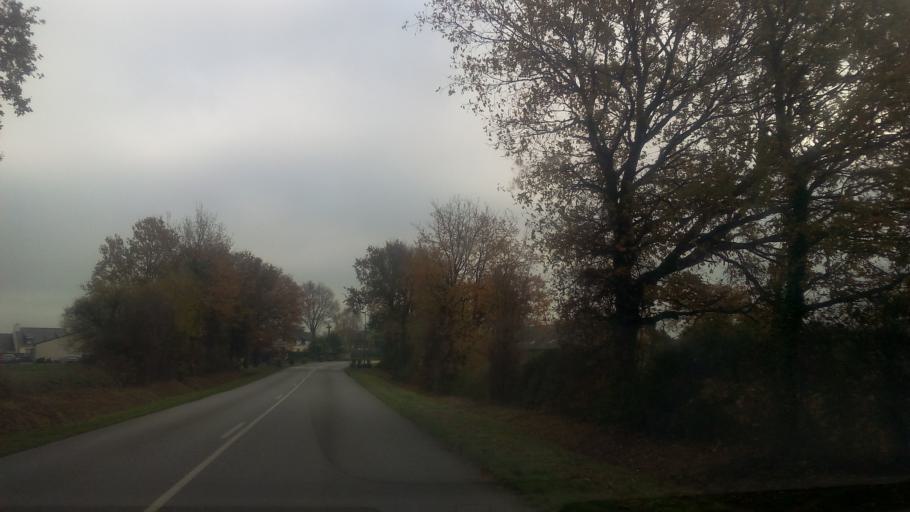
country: FR
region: Brittany
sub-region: Departement du Morbihan
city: Saint-Vincent-sur-Oust
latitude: 47.7029
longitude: -2.1515
